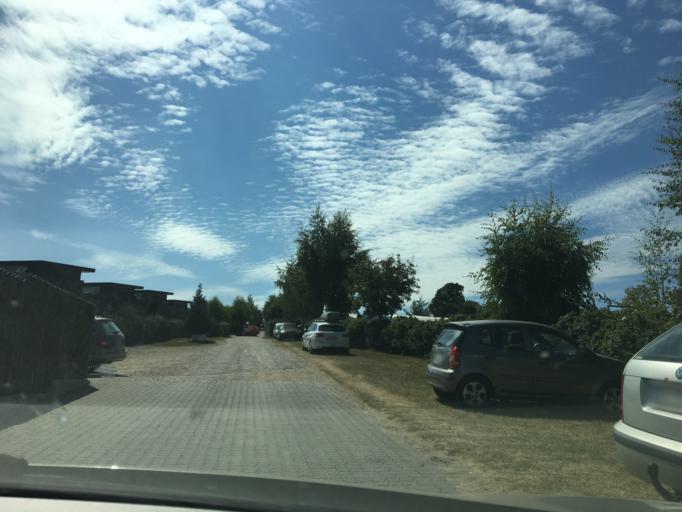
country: DK
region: South Denmark
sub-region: Middelfart Kommune
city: Norre Aby
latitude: 55.5064
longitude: 9.8994
